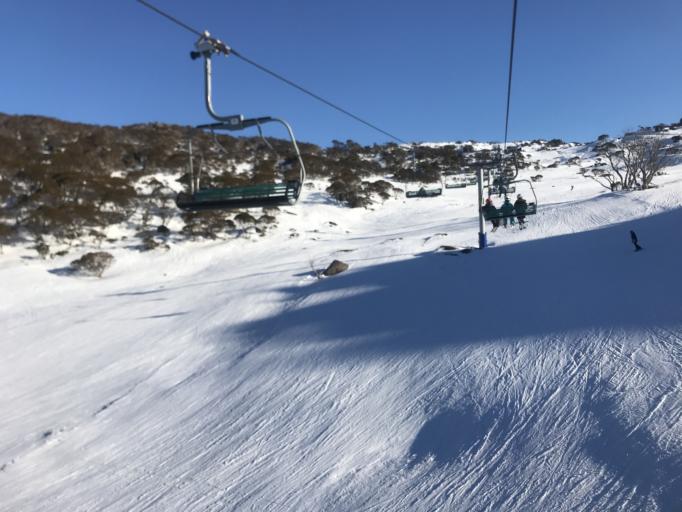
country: AU
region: New South Wales
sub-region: Snowy River
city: Jindabyne
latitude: -36.3893
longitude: 148.3972
